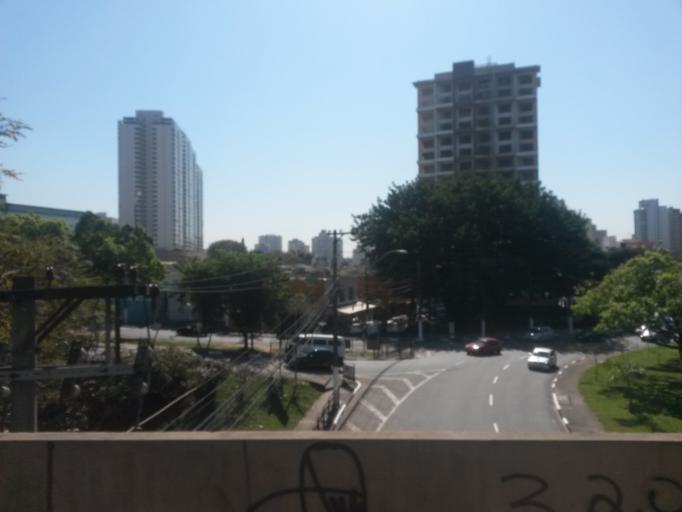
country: BR
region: Sao Paulo
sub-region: Sao Bernardo Do Campo
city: Sao Bernardo do Campo
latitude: -23.6899
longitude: -46.5610
